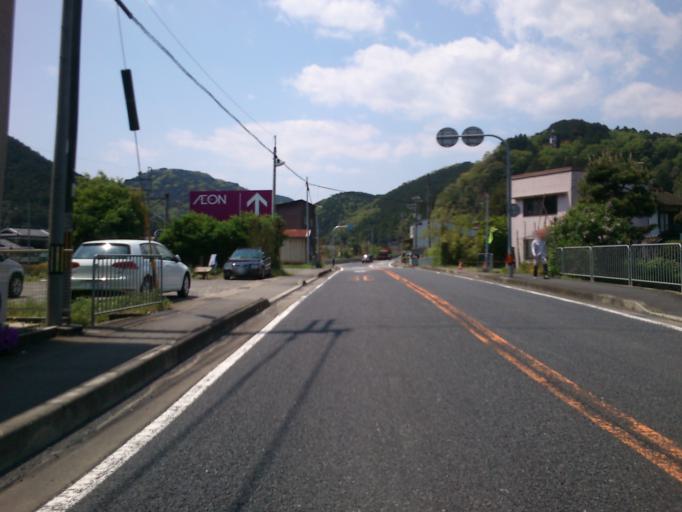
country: JP
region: Kyoto
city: Fukuchiyama
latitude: 35.3205
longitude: 134.9966
